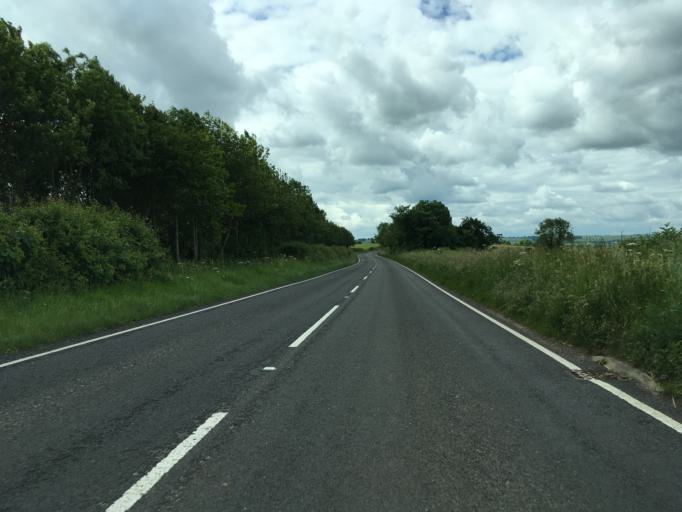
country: GB
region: England
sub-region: Oxfordshire
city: Shipton under Wychwood
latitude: 51.8802
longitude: -1.5741
